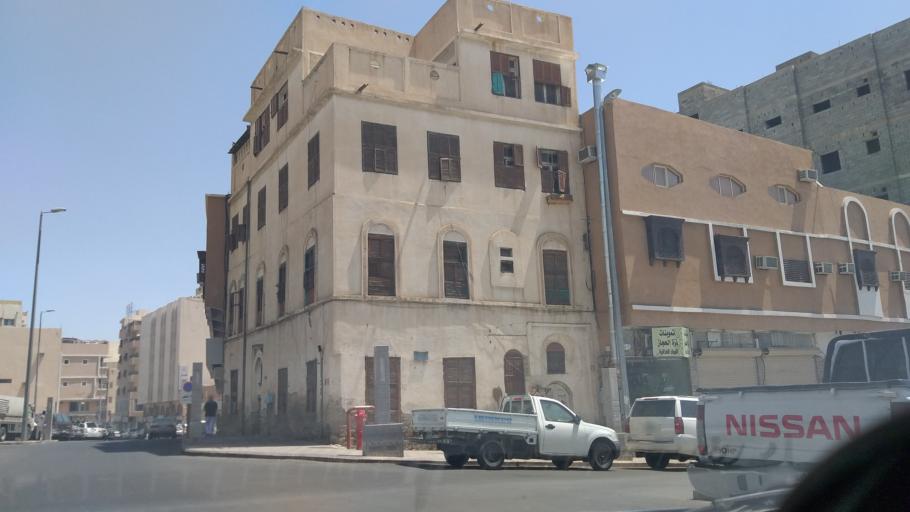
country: SA
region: Makkah
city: Ta'if
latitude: 21.2709
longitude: 40.4072
